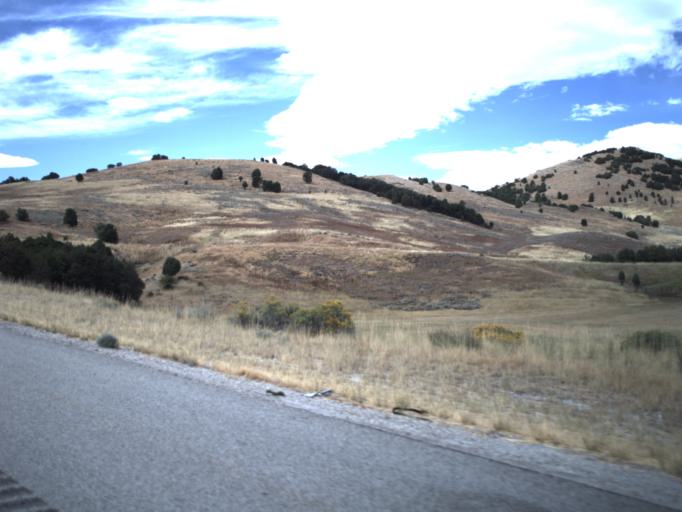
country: US
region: Utah
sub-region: Box Elder County
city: Brigham City
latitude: 41.5284
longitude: -111.9517
